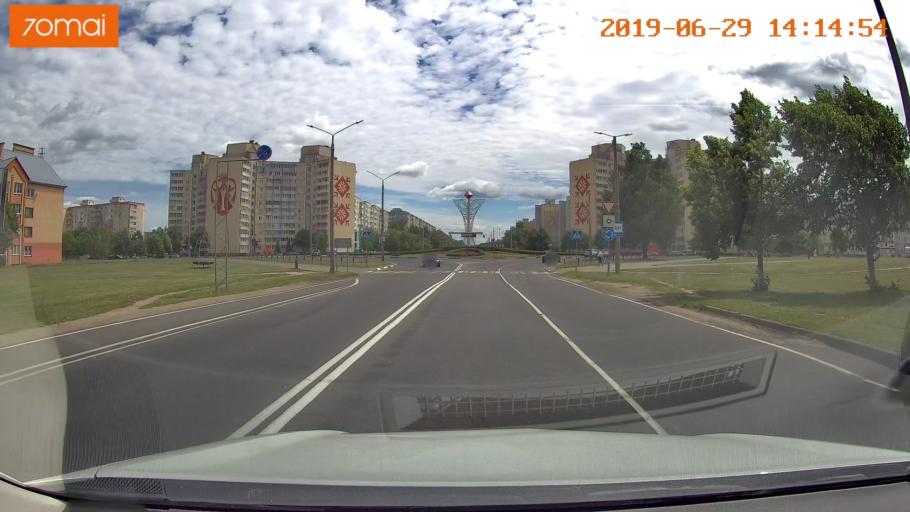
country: BY
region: Minsk
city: Salihorsk
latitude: 52.7929
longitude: 27.5192
